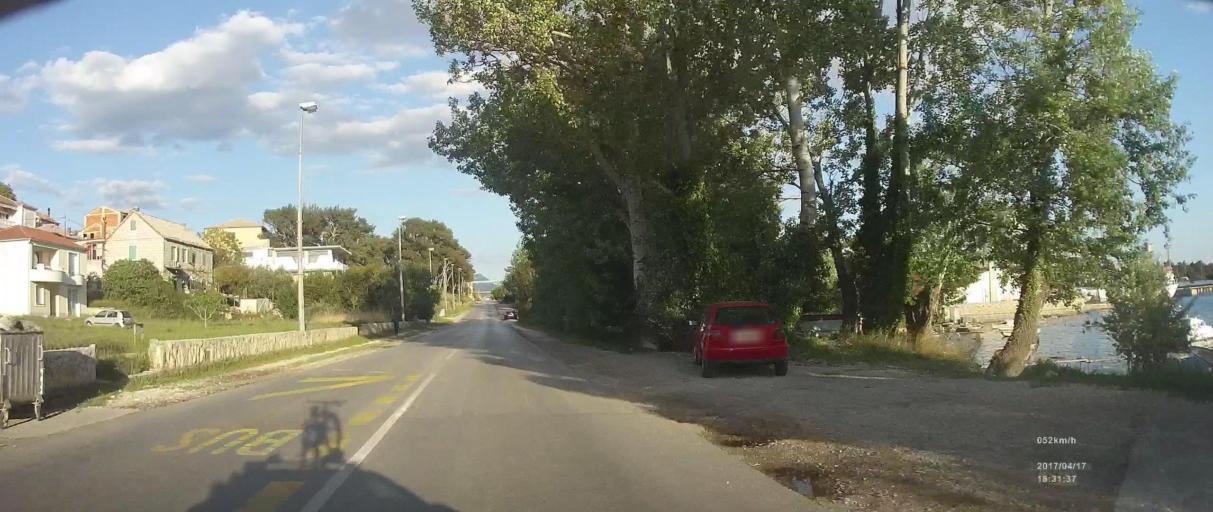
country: HR
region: Splitsko-Dalmatinska
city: Vranjic
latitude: 43.5446
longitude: 16.4362
